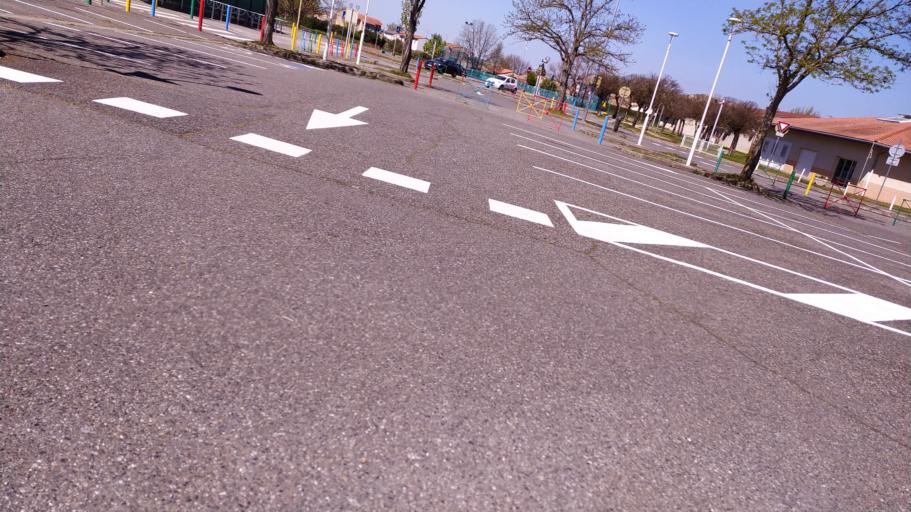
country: FR
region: Midi-Pyrenees
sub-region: Departement de la Haute-Garonne
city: Tournefeuille
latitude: 43.5891
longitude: 1.3163
